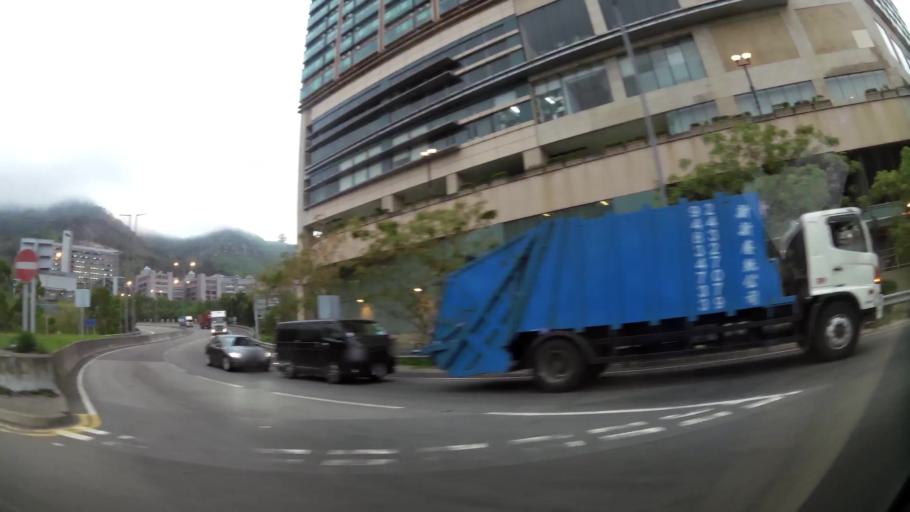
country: HK
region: Tsuen Wan
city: Tsuen Wan
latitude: 22.3414
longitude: 114.1100
